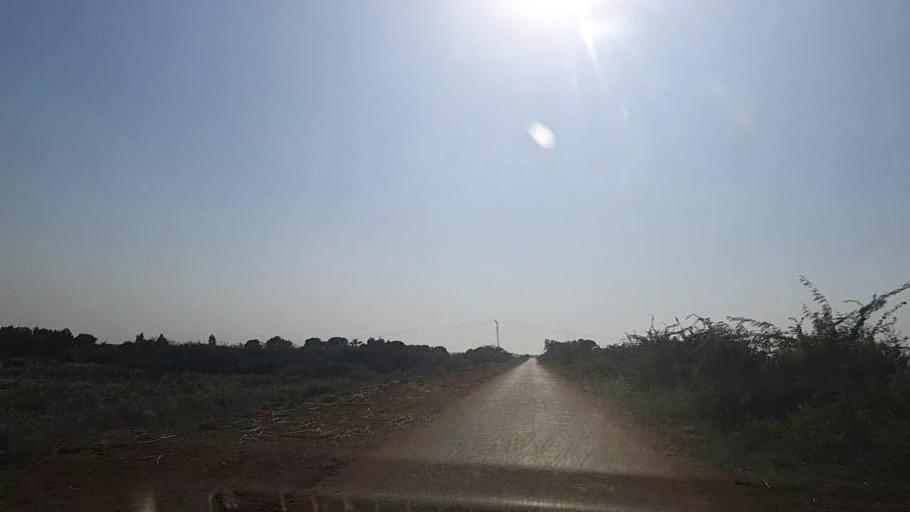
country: PK
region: Sindh
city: Daro Mehar
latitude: 25.0018
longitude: 68.1204
